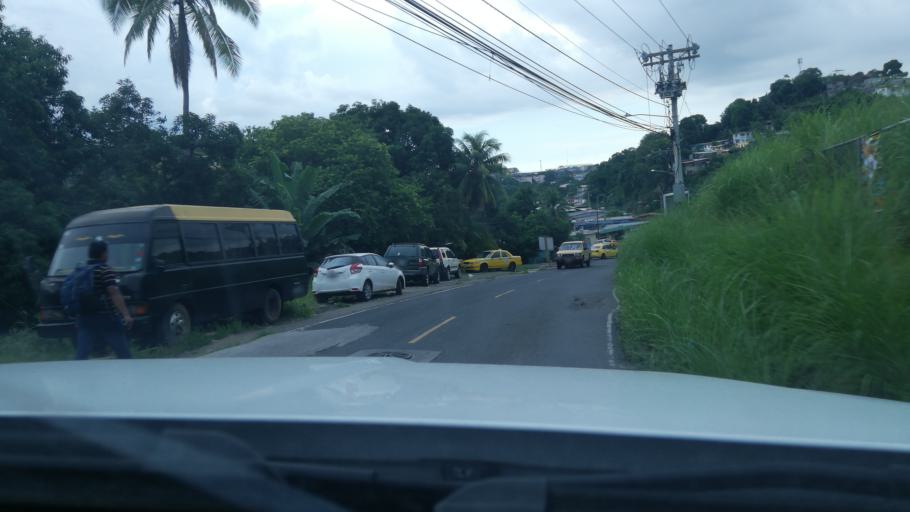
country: PA
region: Panama
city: San Miguelito
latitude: 9.0485
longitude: -79.4928
